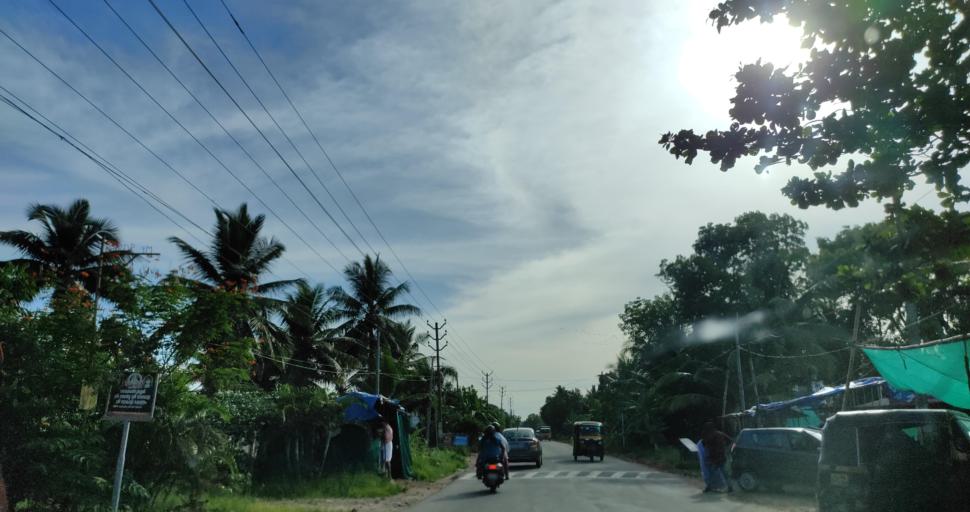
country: IN
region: Kerala
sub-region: Kottayam
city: Kottayam
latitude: 9.5923
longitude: 76.4485
